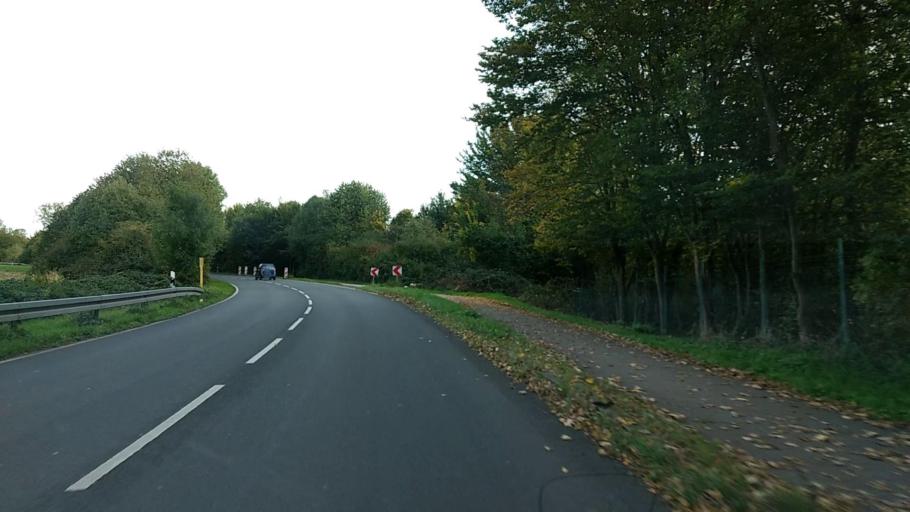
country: DE
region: North Rhine-Westphalia
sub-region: Regierungsbezirk Koln
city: Bergheim
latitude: 50.9396
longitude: 6.6586
